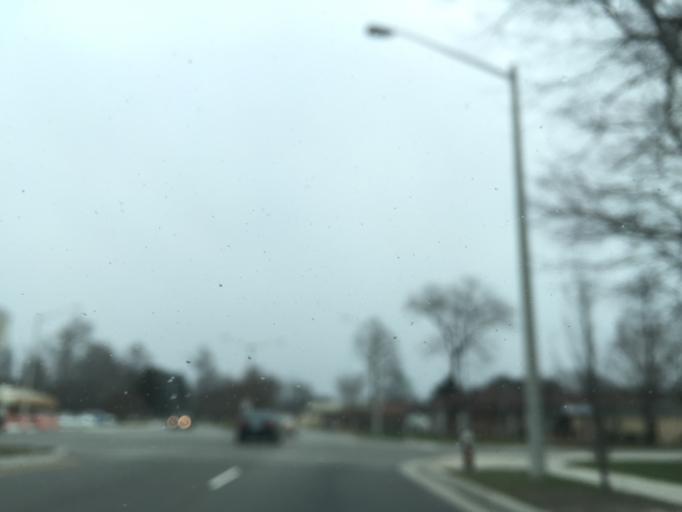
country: US
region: Virginia
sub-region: City of Newport News
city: Newport News
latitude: 37.0889
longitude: -76.4817
